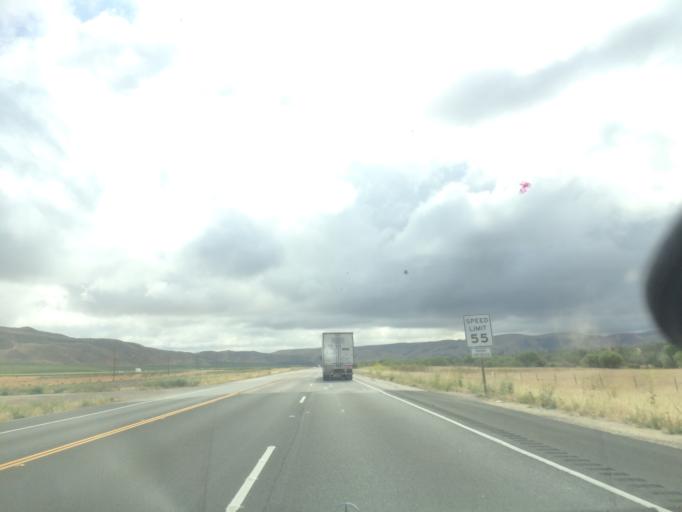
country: US
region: California
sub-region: San Luis Obispo County
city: Shandon
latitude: 35.6620
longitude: -120.4009
